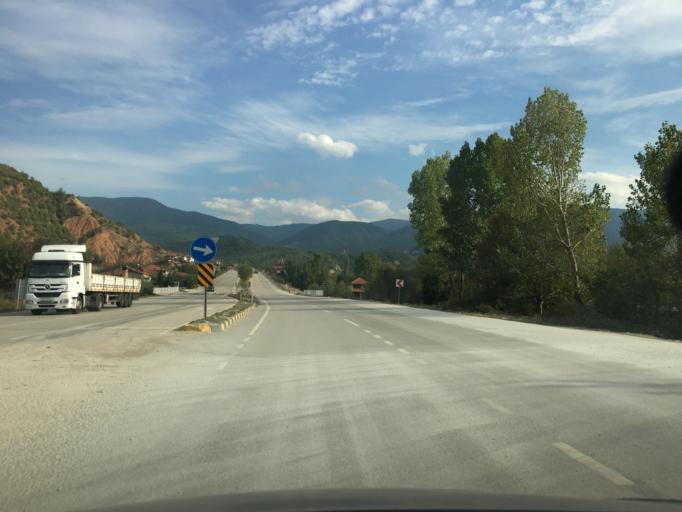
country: TR
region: Karabuk
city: Karabuk
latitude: 41.1004
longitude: 32.6708
